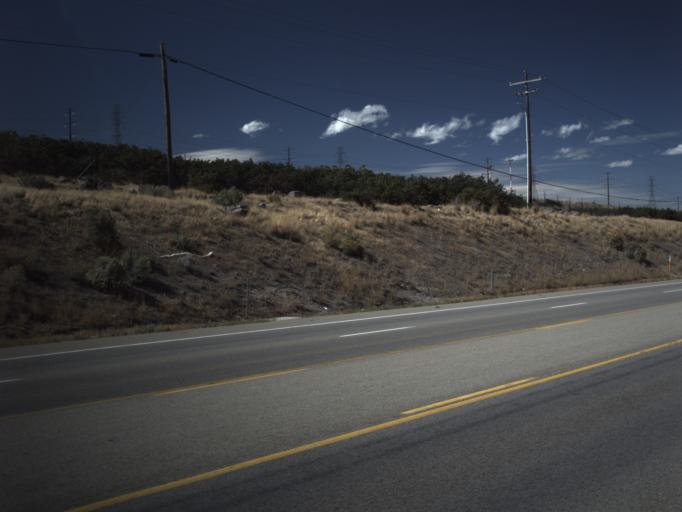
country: US
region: Utah
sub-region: Salt Lake County
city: Bluffdale
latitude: 40.4475
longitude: -111.9357
